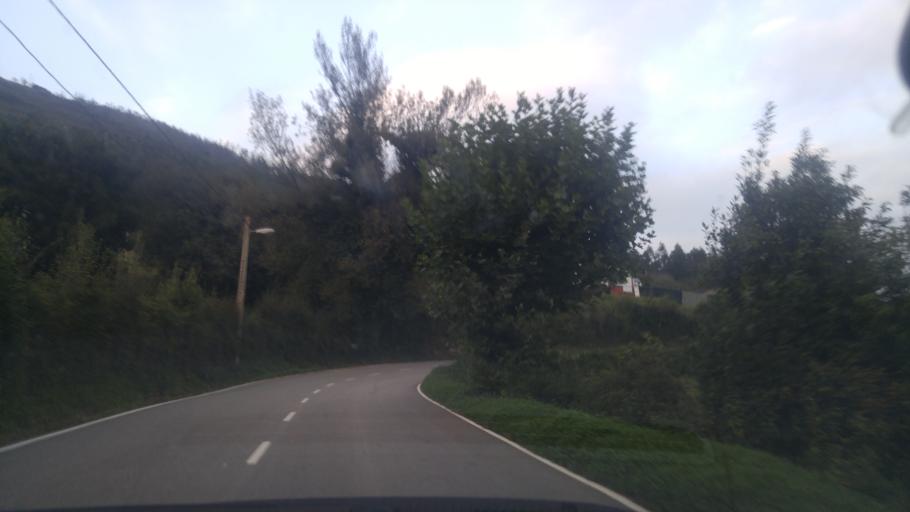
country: ES
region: Asturias
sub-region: Province of Asturias
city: Oviedo
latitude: 43.3782
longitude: -5.8652
